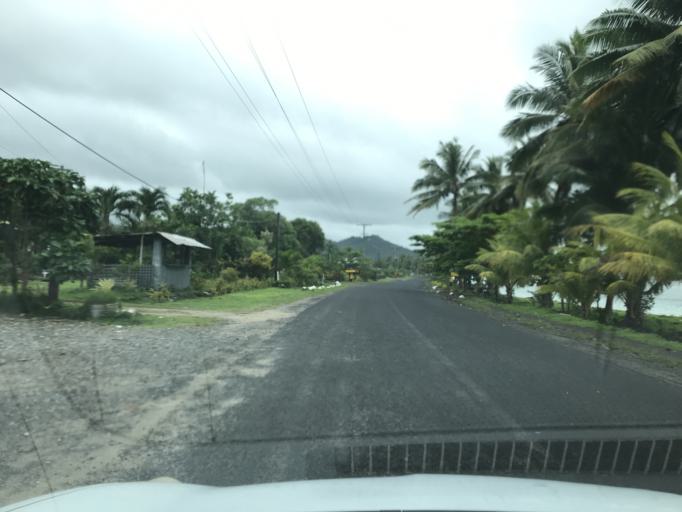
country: WS
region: Atua
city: Solosolo
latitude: -13.8627
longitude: -171.6774
